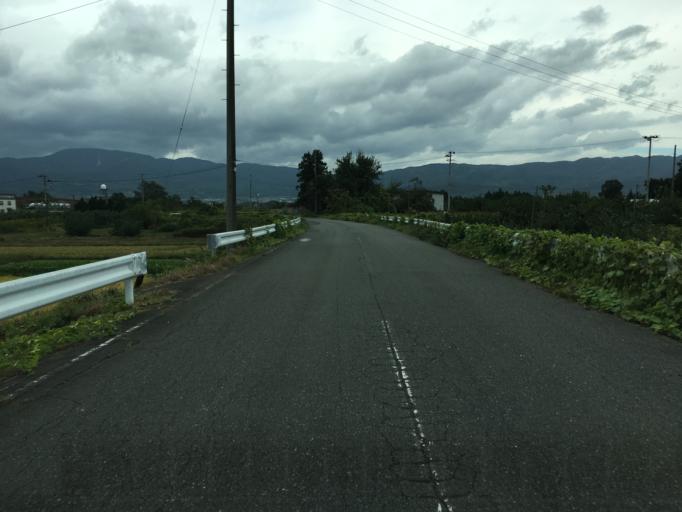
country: JP
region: Fukushima
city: Yanagawamachi-saiwaicho
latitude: 37.8483
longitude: 140.5698
